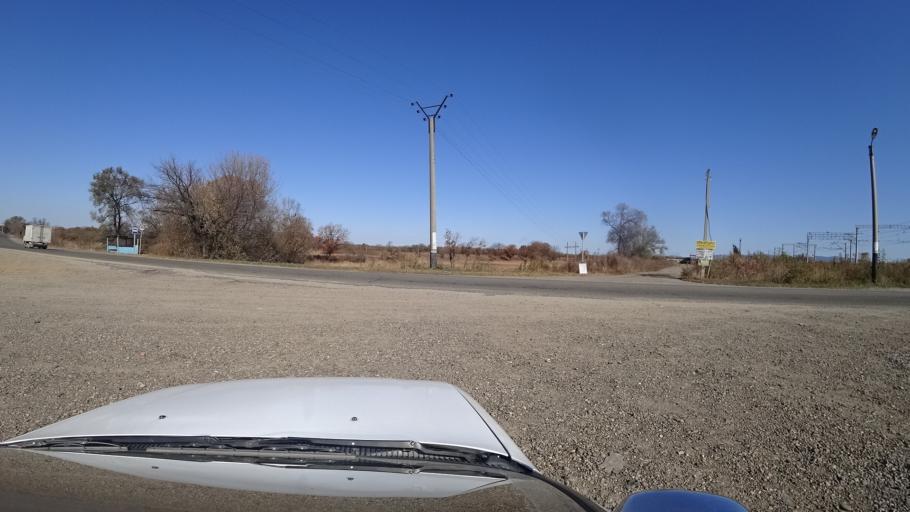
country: RU
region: Primorskiy
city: Dal'nerechensk
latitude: 45.9122
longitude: 133.7939
